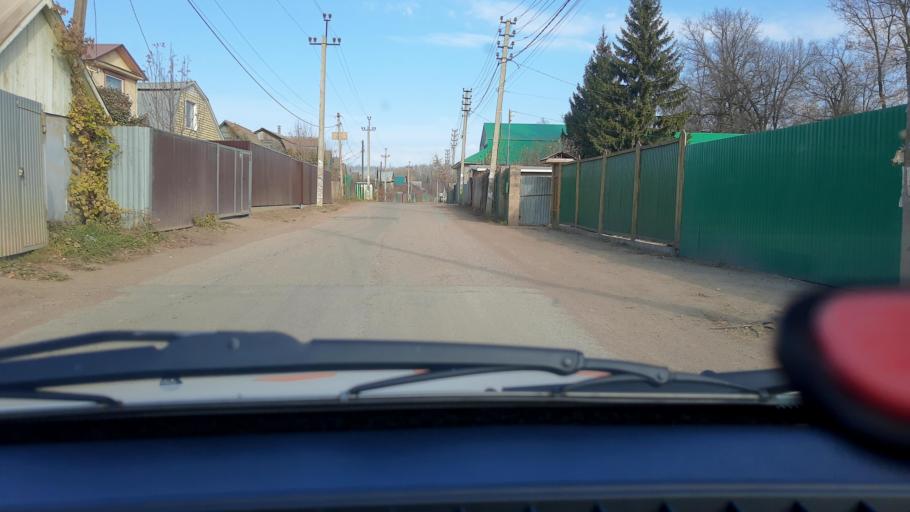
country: RU
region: Bashkortostan
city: Ufa
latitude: 54.6922
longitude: 55.9006
